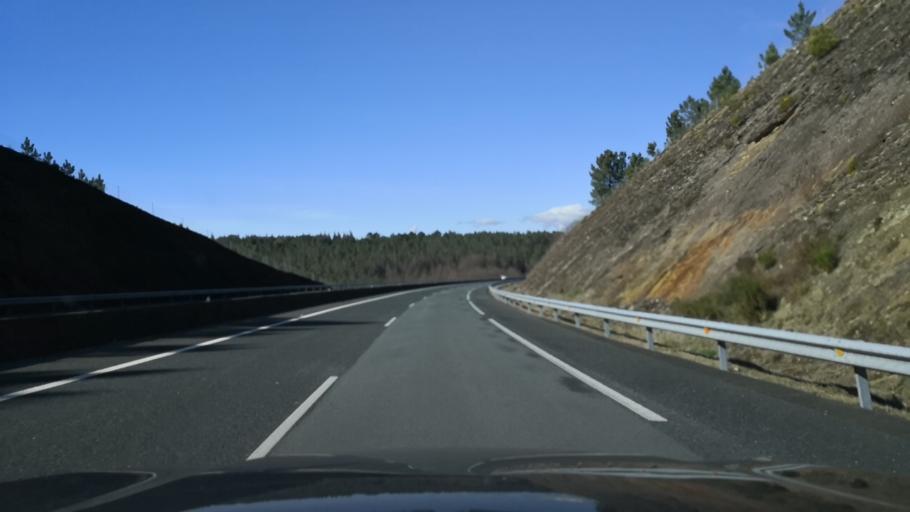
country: ES
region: Galicia
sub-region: Provincia de Pontevedra
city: Lalin
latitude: 42.6032
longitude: -8.0979
